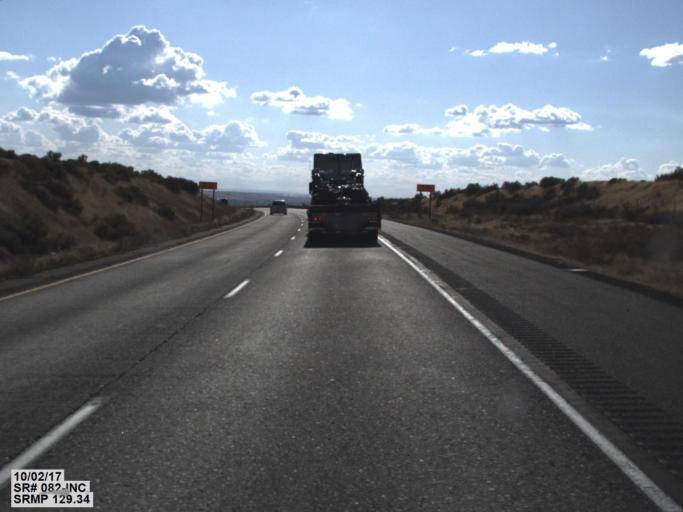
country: US
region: Oregon
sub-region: Umatilla County
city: Umatilla
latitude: 45.9756
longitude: -119.3345
